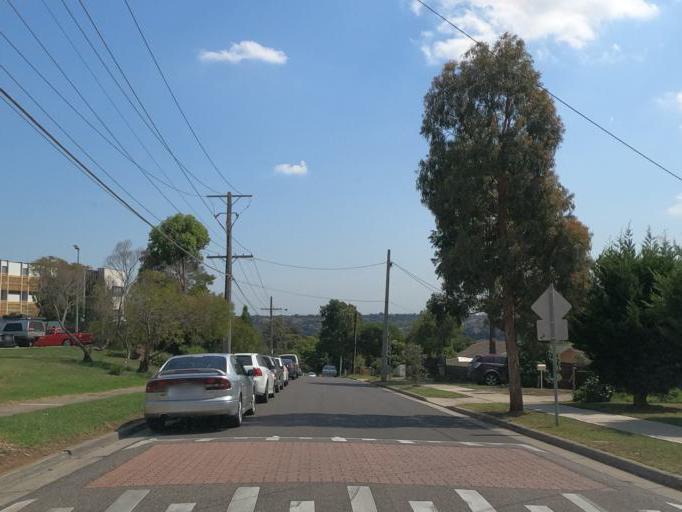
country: AU
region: Victoria
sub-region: Hume
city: Broadmeadows
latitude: -37.6767
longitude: 144.9152
